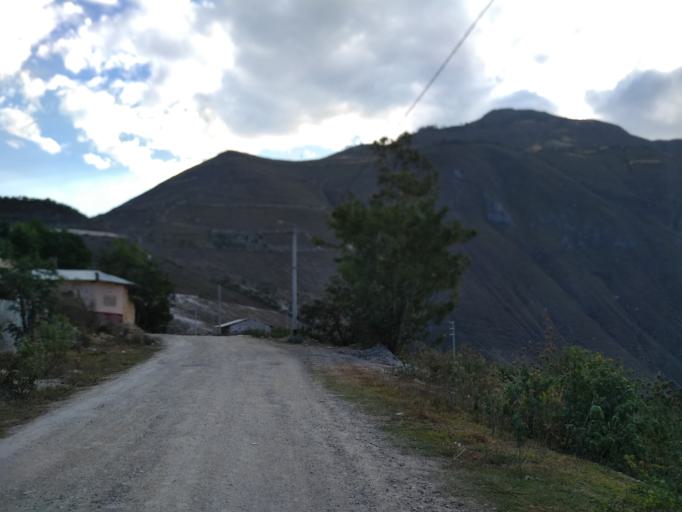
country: PE
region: Amazonas
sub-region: Provincia de Luya
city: Tingo
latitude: -6.3715
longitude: -77.9113
